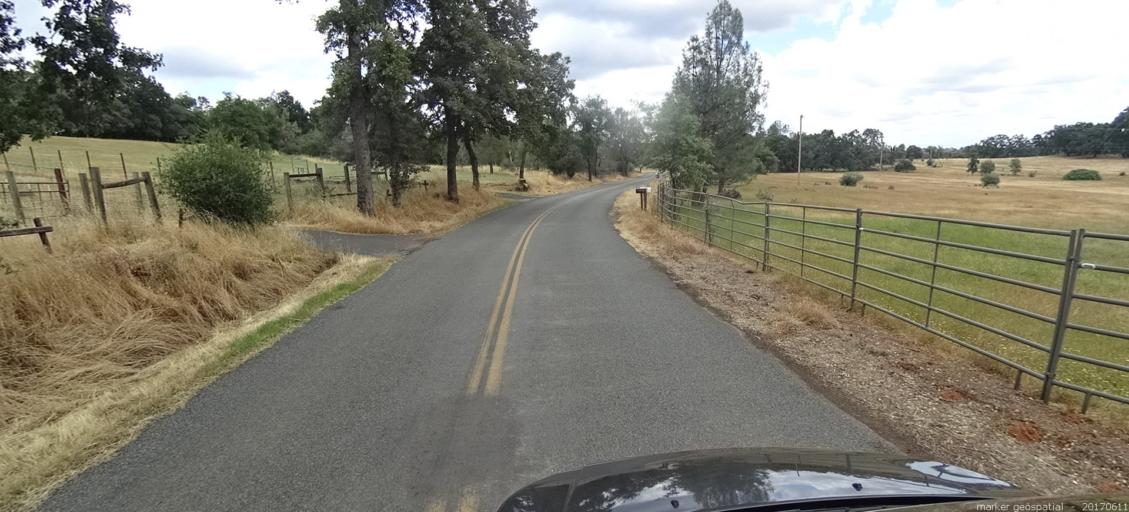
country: US
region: California
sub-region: Butte County
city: Oroville
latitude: 39.6089
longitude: -121.5294
